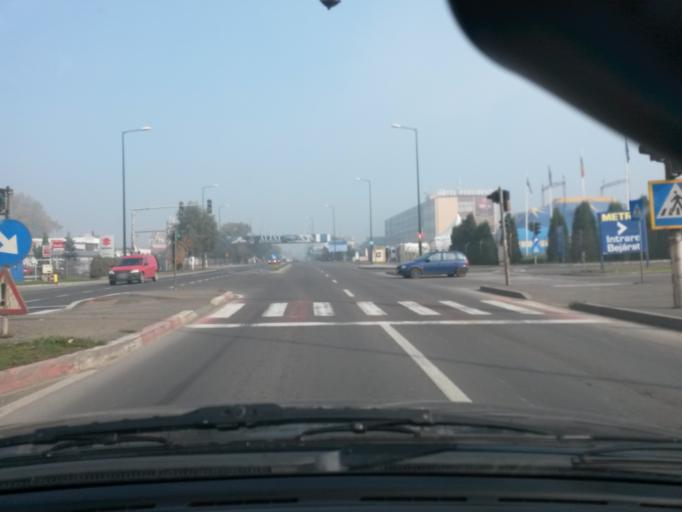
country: RO
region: Mures
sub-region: Comuna Sancraiu de Mures
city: Nazna
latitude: 46.5148
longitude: 24.5173
